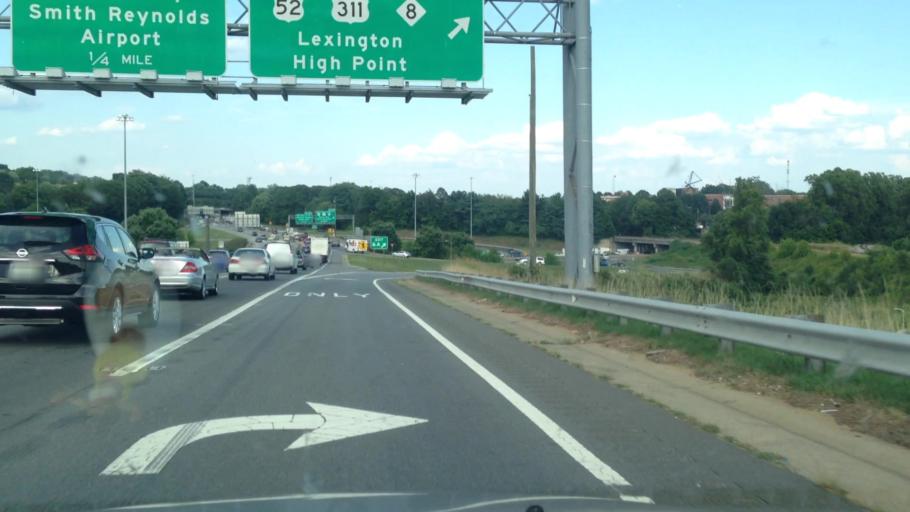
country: US
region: North Carolina
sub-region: Forsyth County
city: Winston-Salem
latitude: 36.0935
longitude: -80.2359
